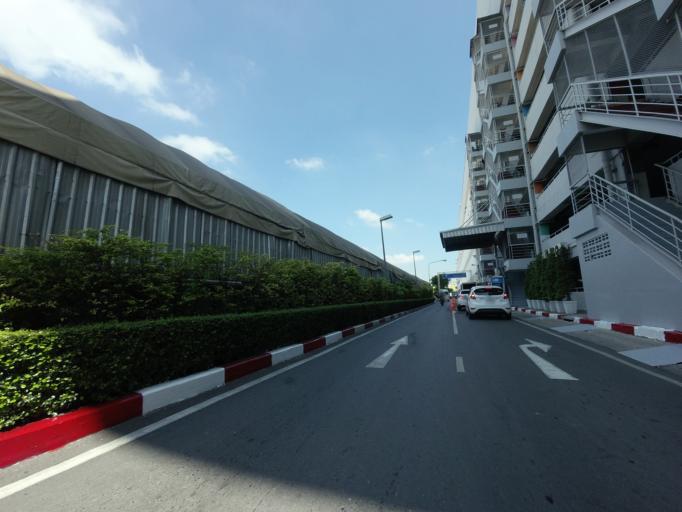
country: TH
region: Bangkok
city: Bang Kapi
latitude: 13.7650
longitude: 100.6419
